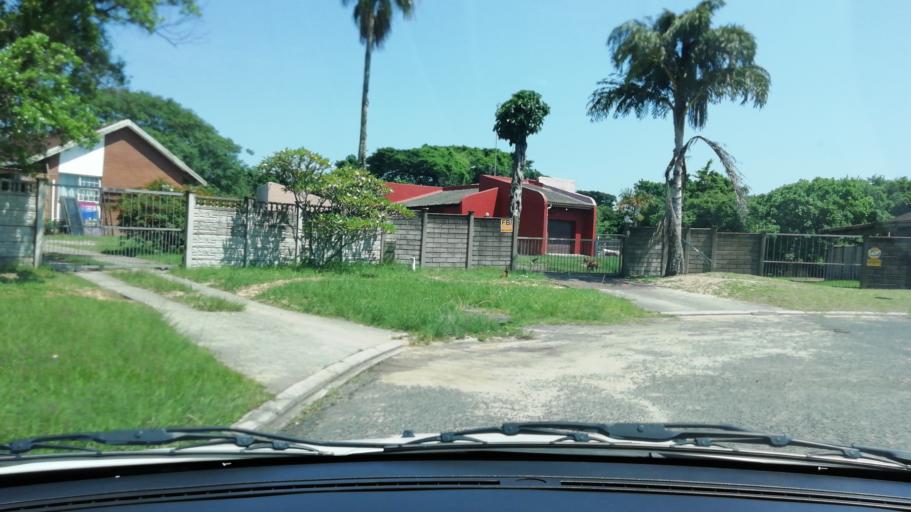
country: ZA
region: KwaZulu-Natal
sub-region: uThungulu District Municipality
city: Richards Bay
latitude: -28.7382
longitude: 32.0596
